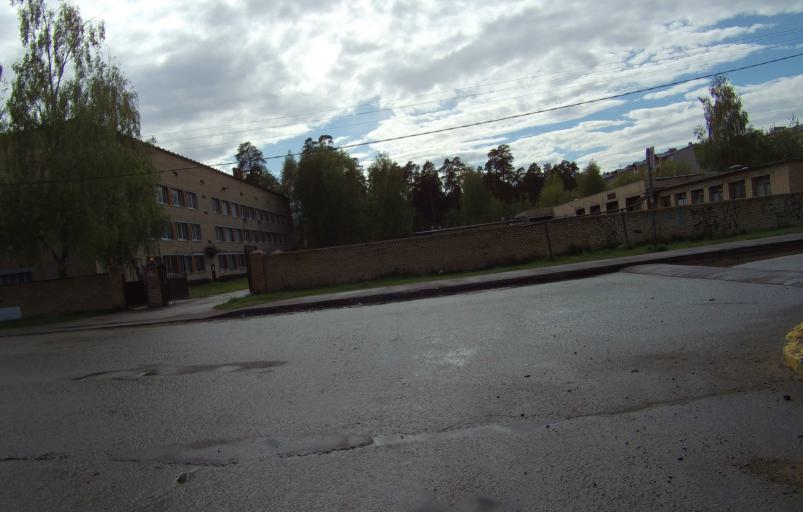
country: RU
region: Moskovskaya
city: Ramenskoye
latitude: 55.5695
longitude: 38.2003
